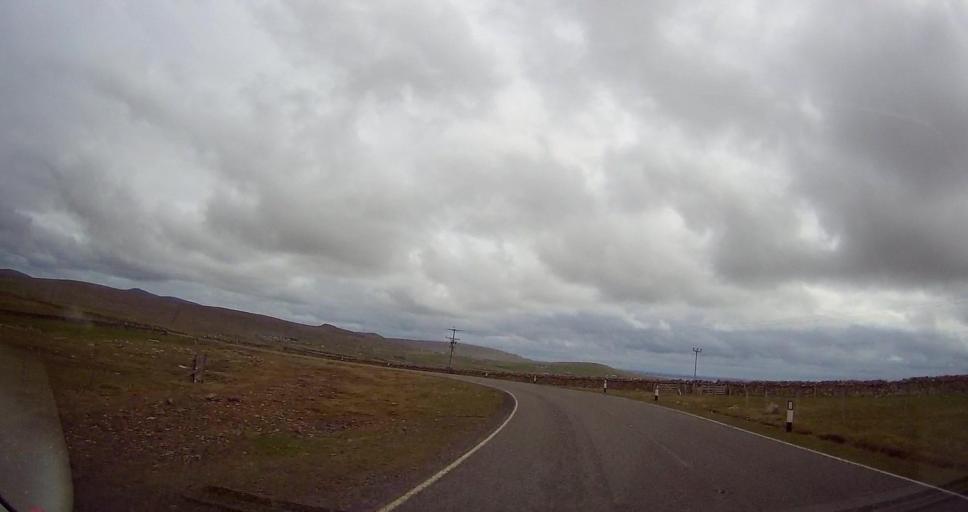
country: GB
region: Scotland
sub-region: Shetland Islands
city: Shetland
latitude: 60.7431
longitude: -0.8865
